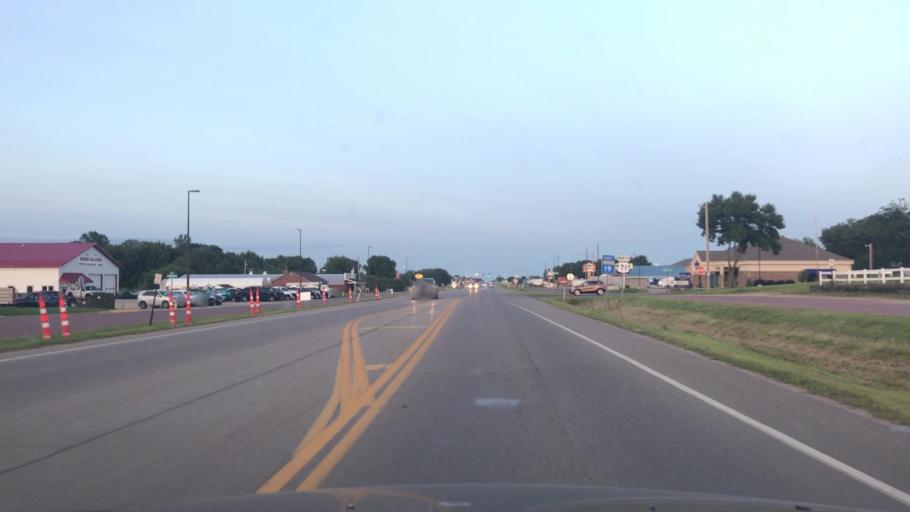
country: US
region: Minnesota
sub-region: Redwood County
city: Redwood Falls
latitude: 44.5414
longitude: -95.1061
